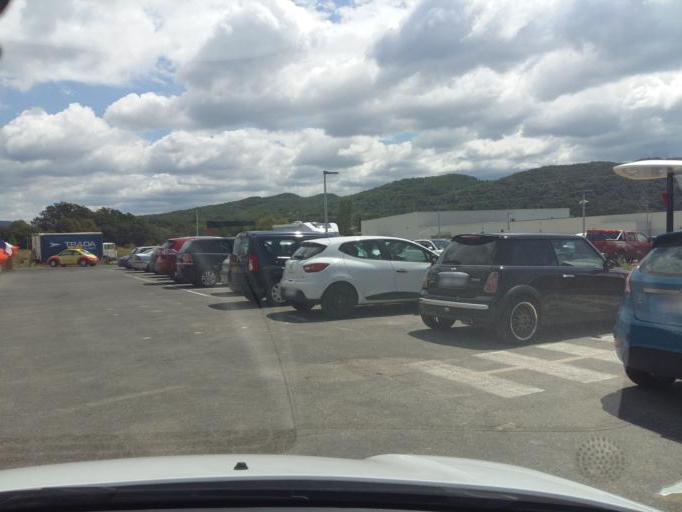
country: FR
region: Provence-Alpes-Cote d'Azur
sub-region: Departement du Vaucluse
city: Vaison-la-Romaine
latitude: 44.2560
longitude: 5.0969
